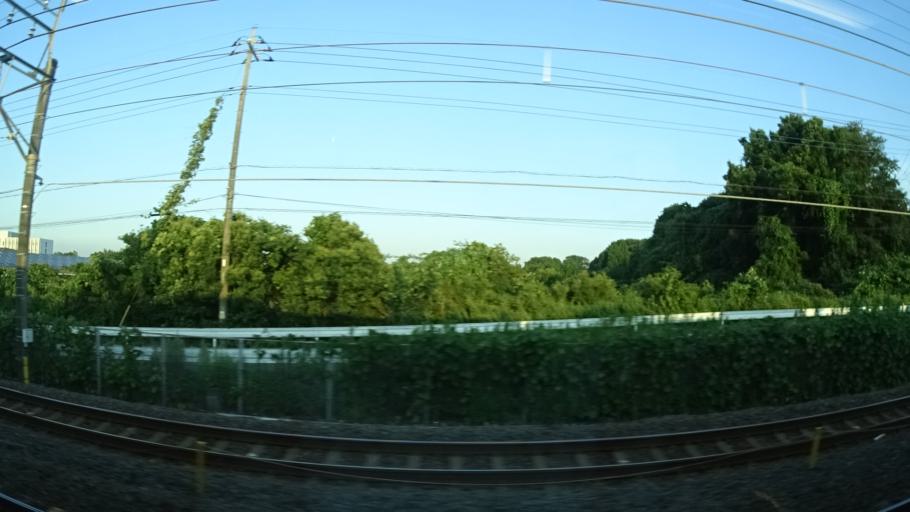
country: JP
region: Chiba
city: Abiko
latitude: 35.8755
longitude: 140.0498
